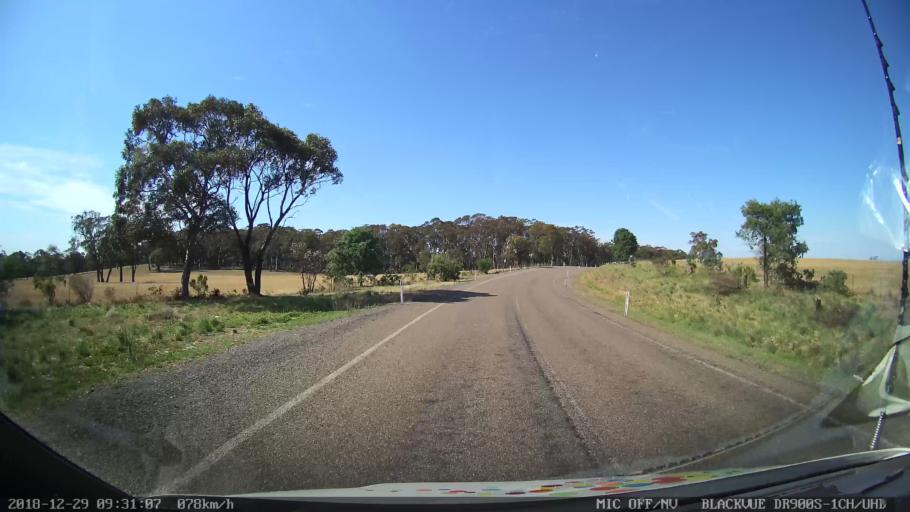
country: AU
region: New South Wales
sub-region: Upper Lachlan Shire
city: Crookwell
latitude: -34.6048
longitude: 149.3653
